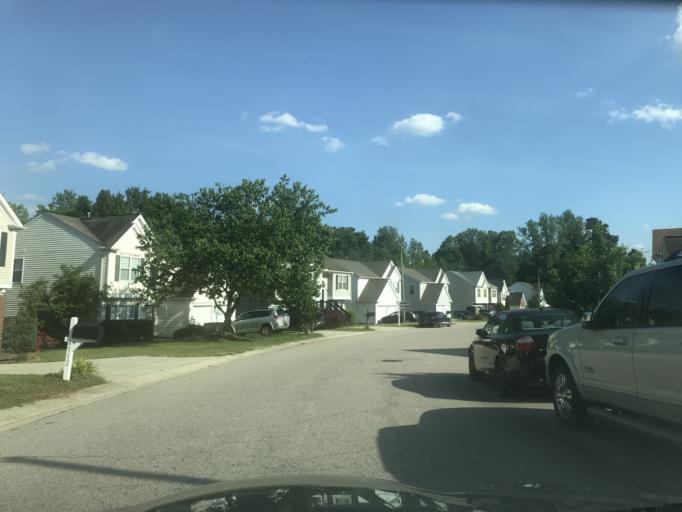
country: US
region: North Carolina
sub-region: Wake County
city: Knightdale
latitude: 35.8433
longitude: -78.5470
